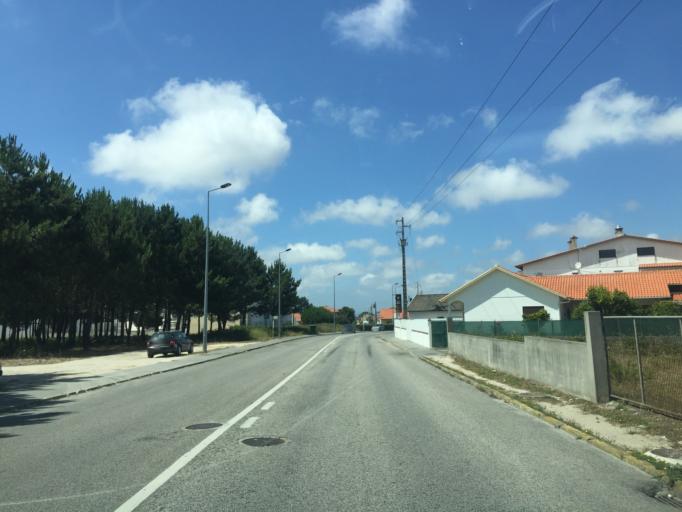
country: PT
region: Leiria
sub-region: Marinha Grande
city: Marinha Grande
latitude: 39.7294
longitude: -8.9299
